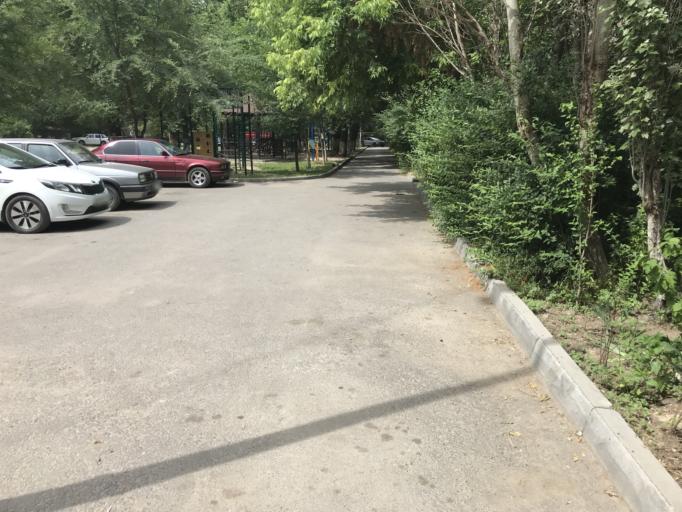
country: KZ
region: Ongtustik Qazaqstan
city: Shymkent
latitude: 42.3109
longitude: 69.5698
